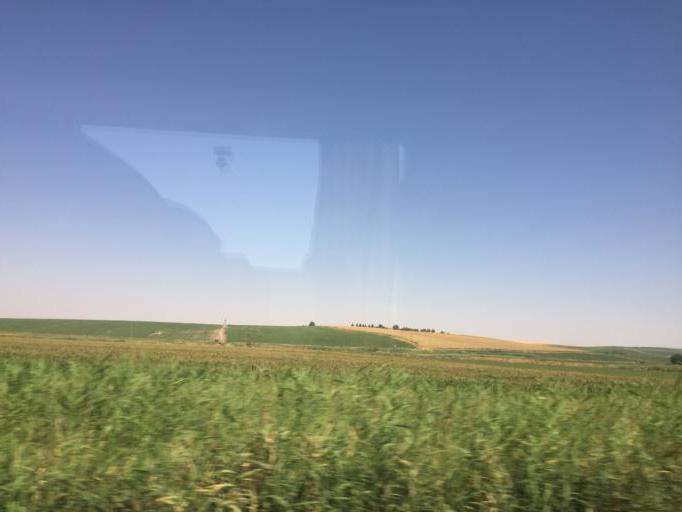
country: TR
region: Diyarbakir
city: Tepe
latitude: 37.8506
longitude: 40.7476
